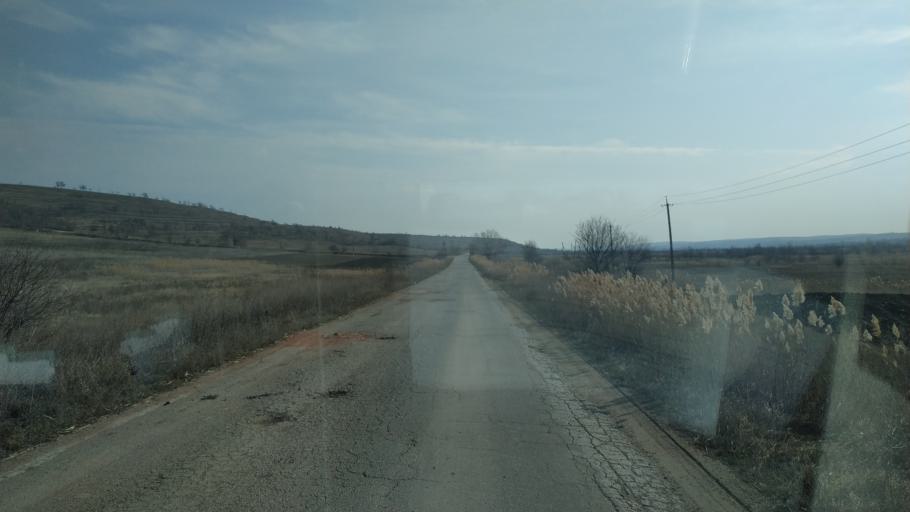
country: MD
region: Chisinau
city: Singera
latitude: 46.9256
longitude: 29.0782
